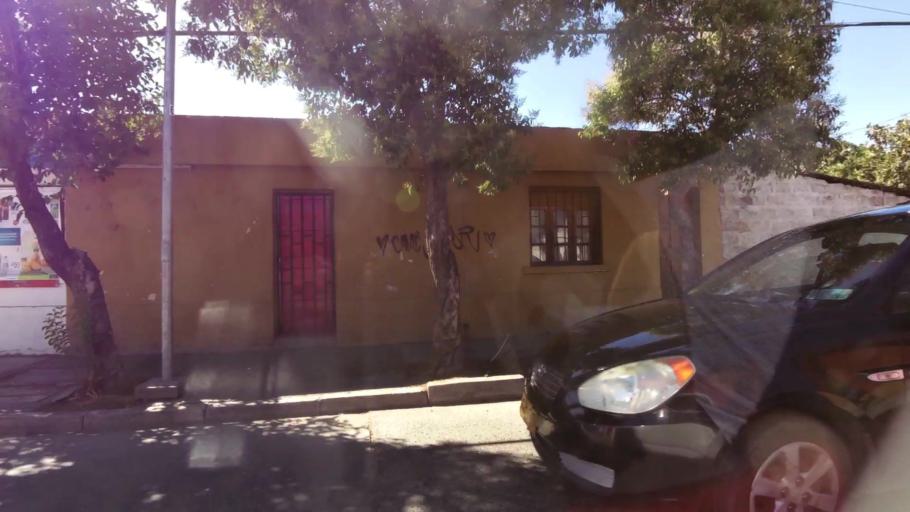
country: CL
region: O'Higgins
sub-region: Provincia de Cachapoal
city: Rancagua
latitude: -34.1772
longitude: -70.7486
